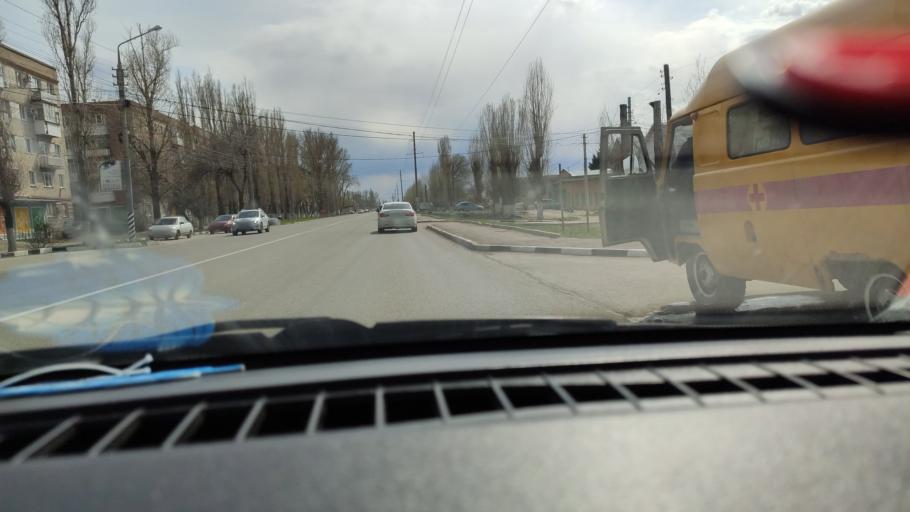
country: RU
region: Saratov
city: Privolzhskiy
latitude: 51.4037
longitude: 46.0379
